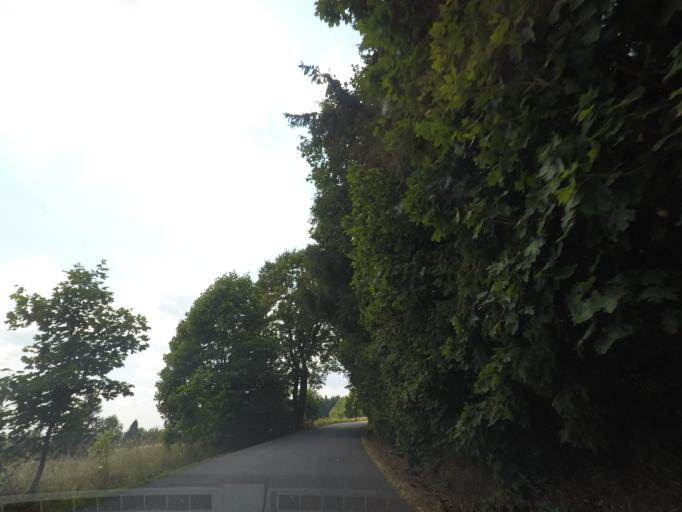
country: CZ
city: Radvanice
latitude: 50.6178
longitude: 16.0647
